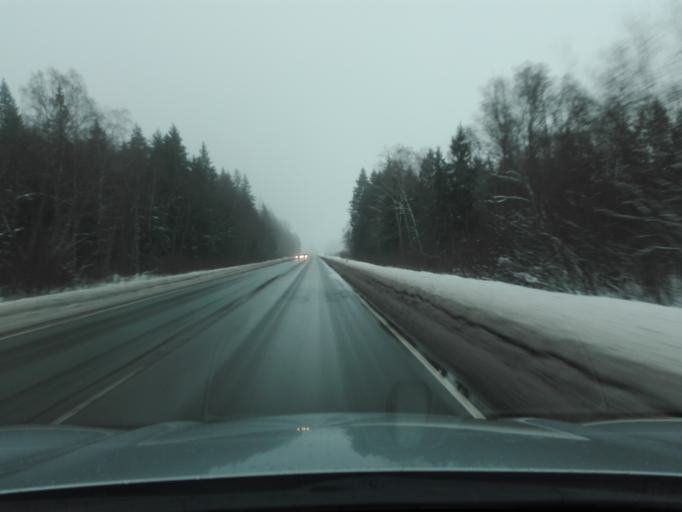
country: EE
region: Raplamaa
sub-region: Kohila vald
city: Kohila
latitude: 59.2388
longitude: 24.7604
